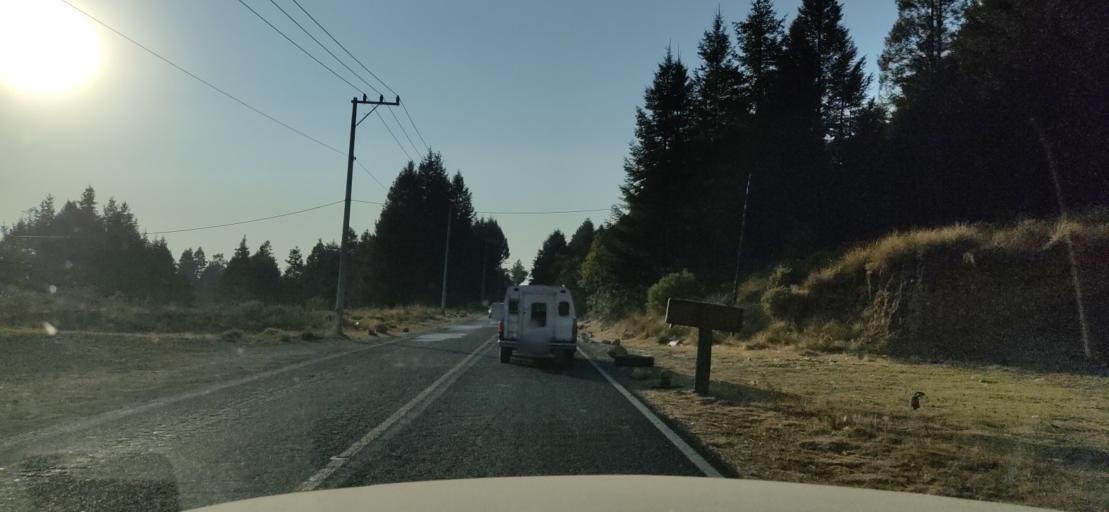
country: MX
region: Mexico
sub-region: Ocoyoacac
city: San Jeronimo Acazulco
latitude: 19.2631
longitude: -99.3726
